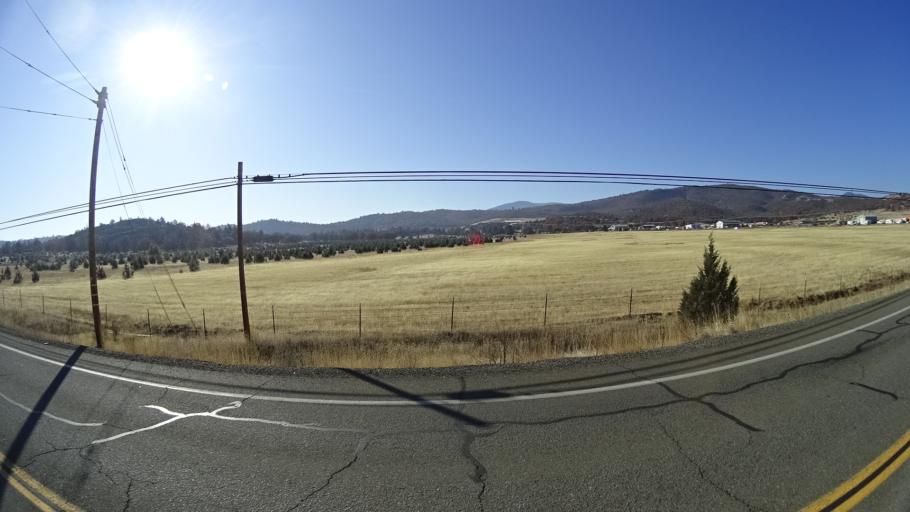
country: US
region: California
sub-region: Siskiyou County
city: Yreka
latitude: 41.7114
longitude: -122.5953
